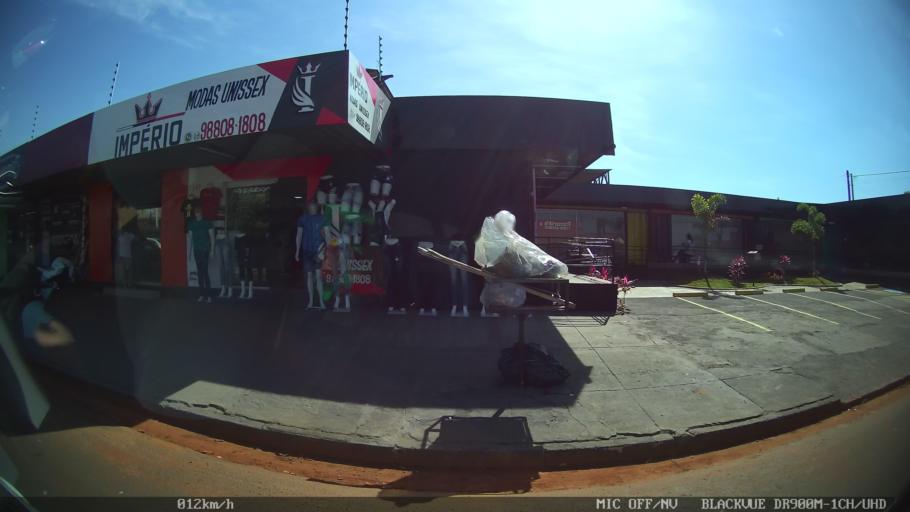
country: BR
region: Sao Paulo
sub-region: Sao Jose Do Rio Preto
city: Sao Jose do Rio Preto
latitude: -20.7835
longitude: -49.3970
